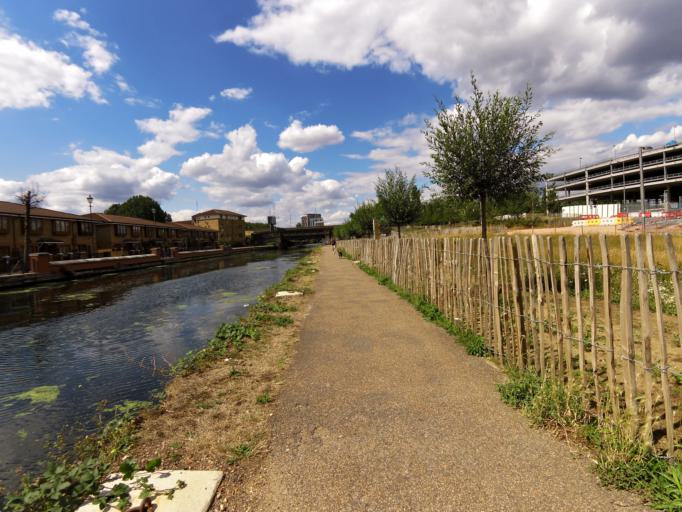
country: GB
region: England
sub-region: Greater London
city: Hackney
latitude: 51.5473
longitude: -0.0254
